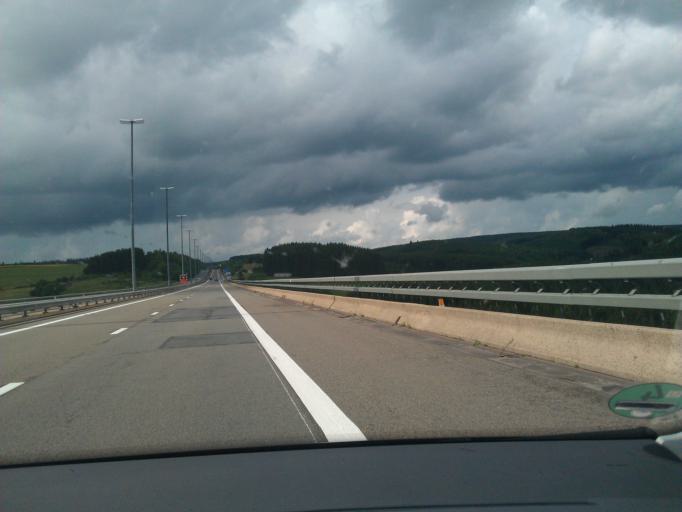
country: DE
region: Rheinland-Pfalz
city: Winterspelt
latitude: 50.2377
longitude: 6.1809
